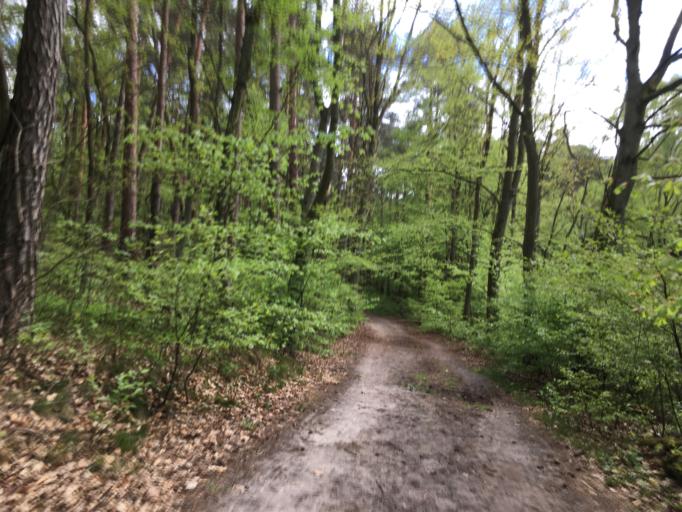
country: DE
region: Brandenburg
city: Rudnitz
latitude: 52.7420
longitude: 13.5888
